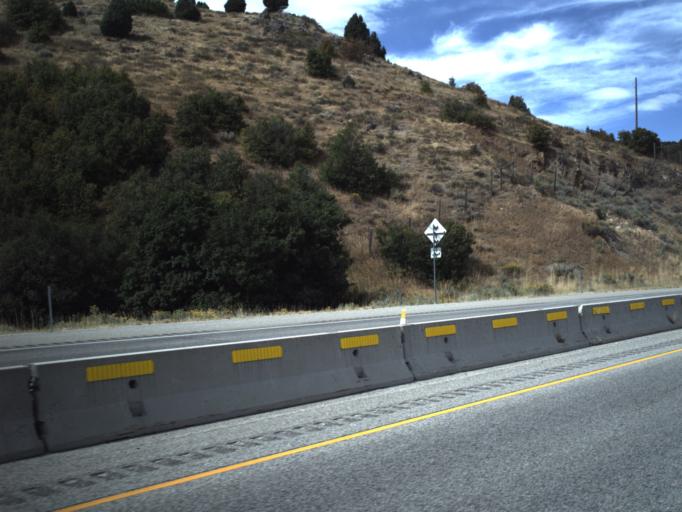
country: US
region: Utah
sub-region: Box Elder County
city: Brigham City
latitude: 41.5346
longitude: -111.9583
